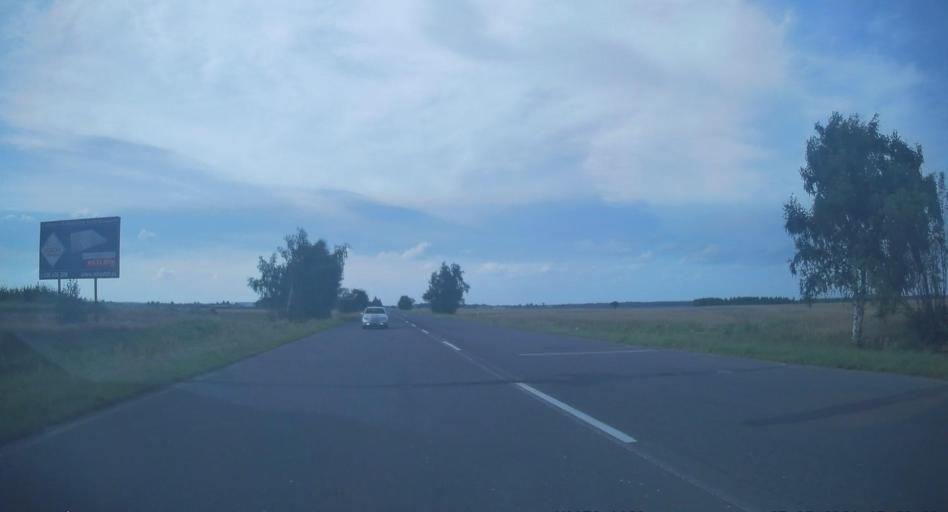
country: PL
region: Lodz Voivodeship
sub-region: Powiat tomaszowski
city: Rzeczyca
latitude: 51.6551
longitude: 20.2752
